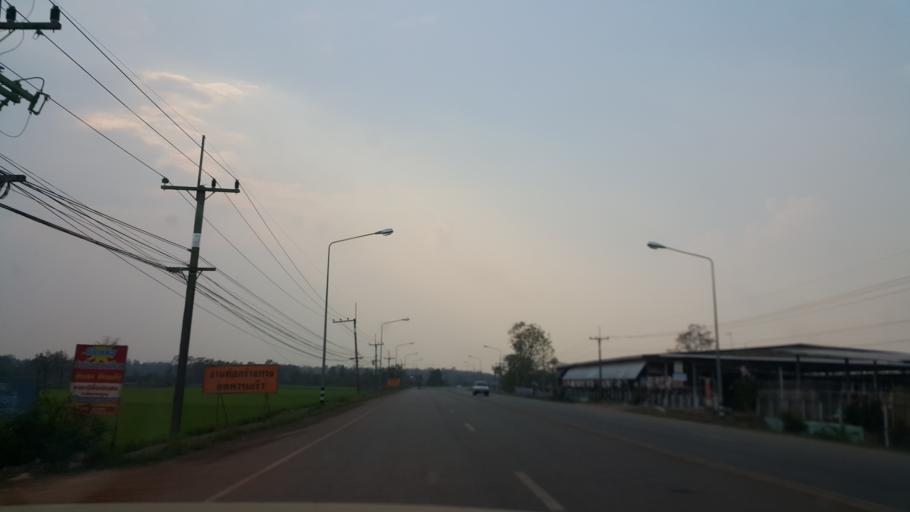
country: TH
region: Nakhon Phanom
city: Renu Nakhon
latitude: 17.0211
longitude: 104.7221
